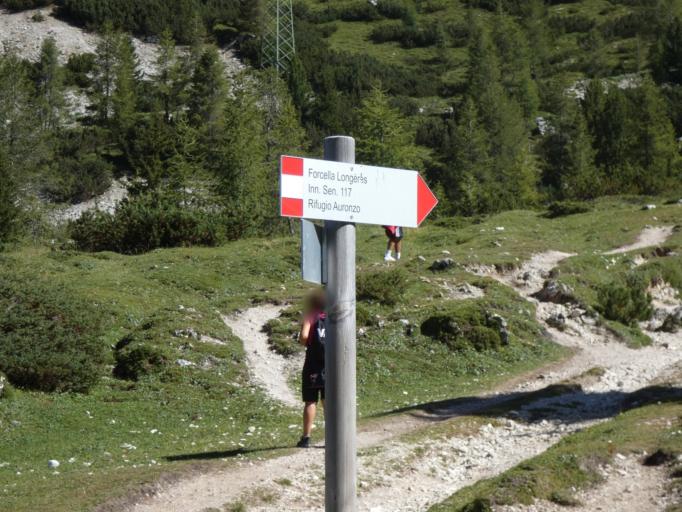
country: IT
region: Trentino-Alto Adige
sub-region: Bolzano
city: Sesto
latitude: 46.6058
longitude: 12.2906
